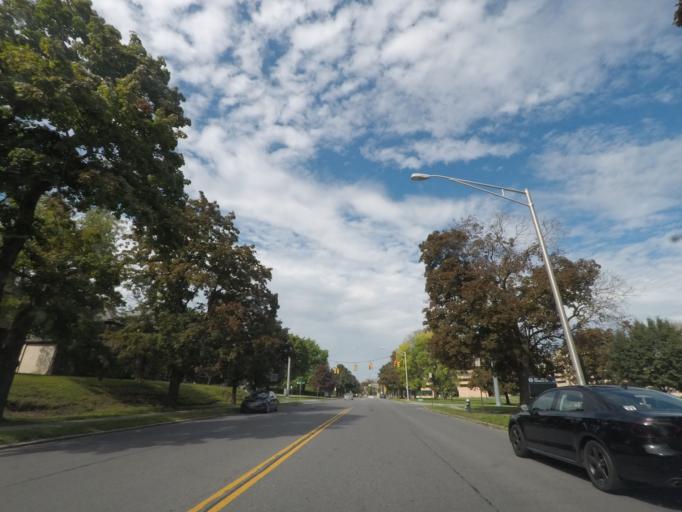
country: US
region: New York
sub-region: Albany County
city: Albany
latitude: 42.6492
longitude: -73.7743
